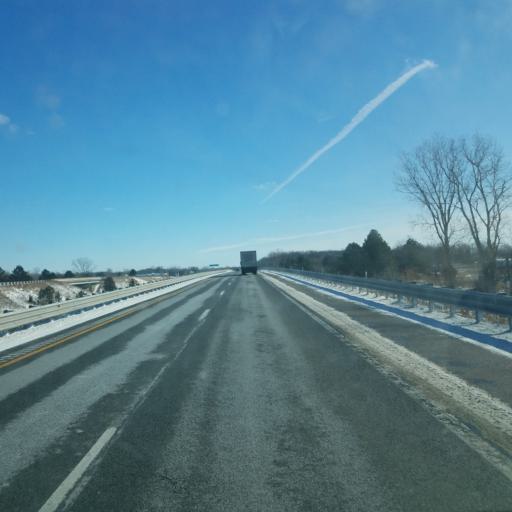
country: US
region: Michigan
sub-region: Ingham County
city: Webberville
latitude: 42.6599
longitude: -84.2003
